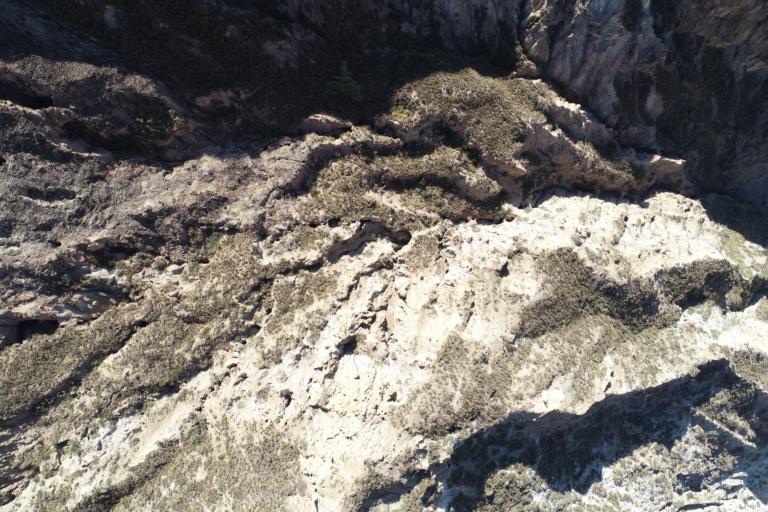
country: BO
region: La Paz
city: La Paz
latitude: -16.5514
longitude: -68.1064
